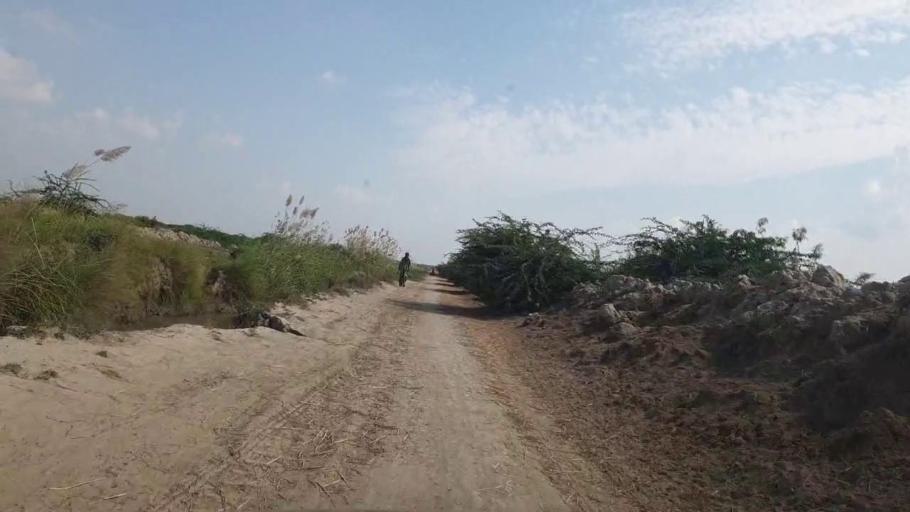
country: PK
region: Sindh
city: Badin
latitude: 24.4774
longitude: 68.5973
